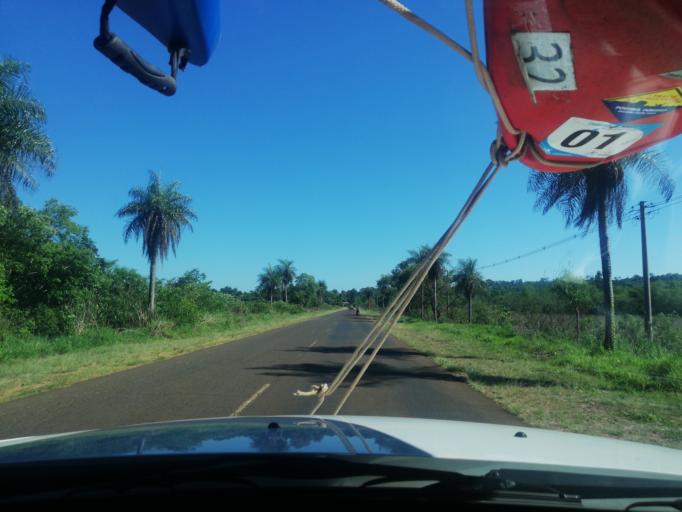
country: AR
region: Misiones
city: Santa Ana
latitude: -27.3431
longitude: -55.5844
